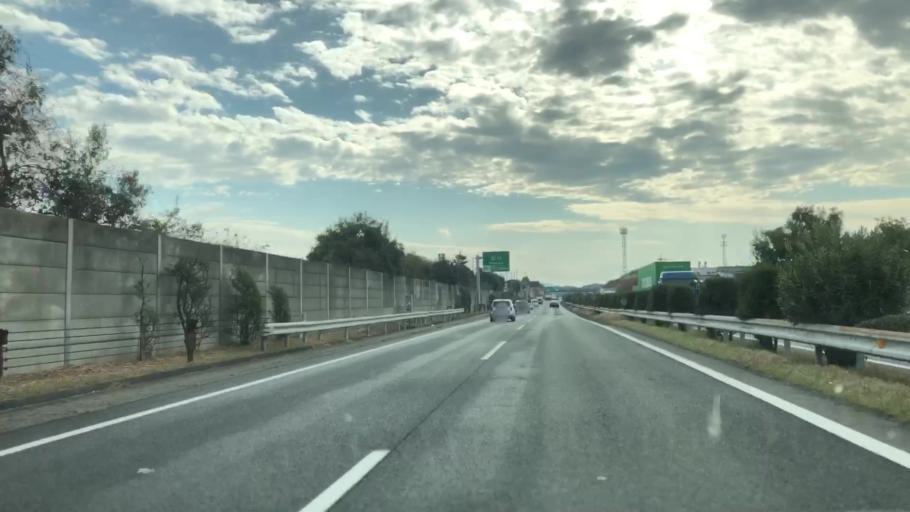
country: JP
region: Fukuoka
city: Kurume
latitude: 33.2626
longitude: 130.5385
